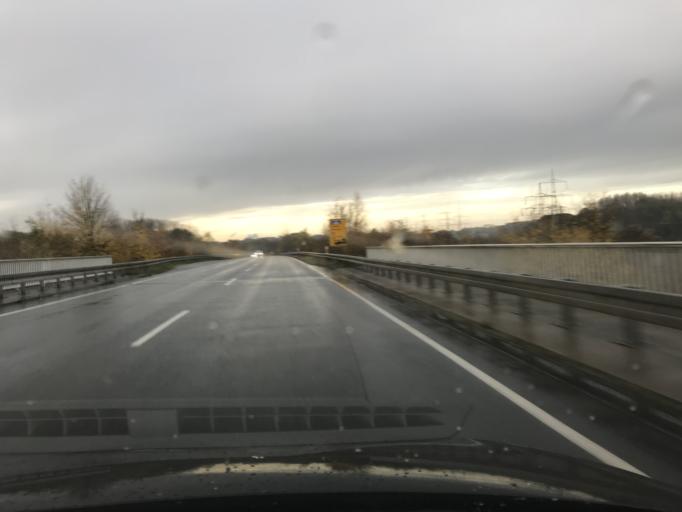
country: DE
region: North Rhine-Westphalia
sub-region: Regierungsbezirk Arnsberg
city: Hamm
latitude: 51.7151
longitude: 7.7554
